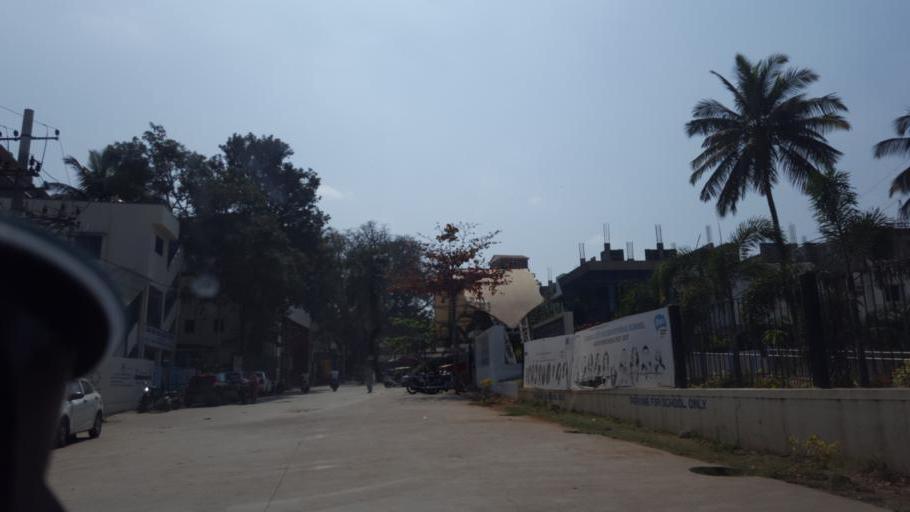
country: IN
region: Karnataka
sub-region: Bangalore Urban
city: Bangalore
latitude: 12.9772
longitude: 77.6722
